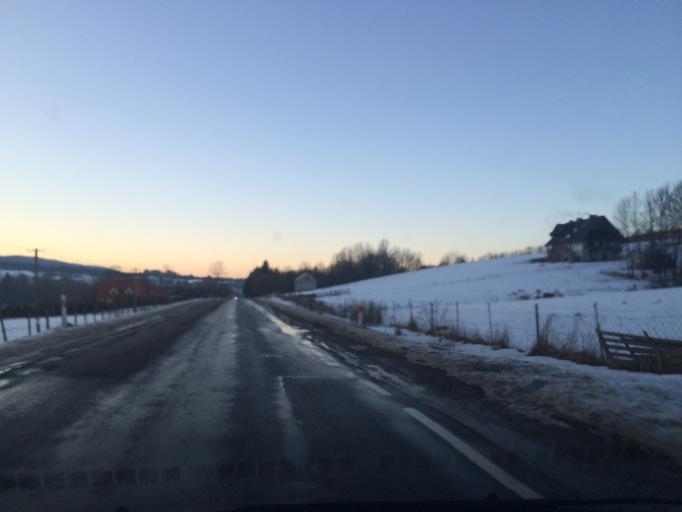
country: PL
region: Subcarpathian Voivodeship
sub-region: Powiat bieszczadzki
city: Czarna
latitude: 49.3690
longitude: 22.6551
